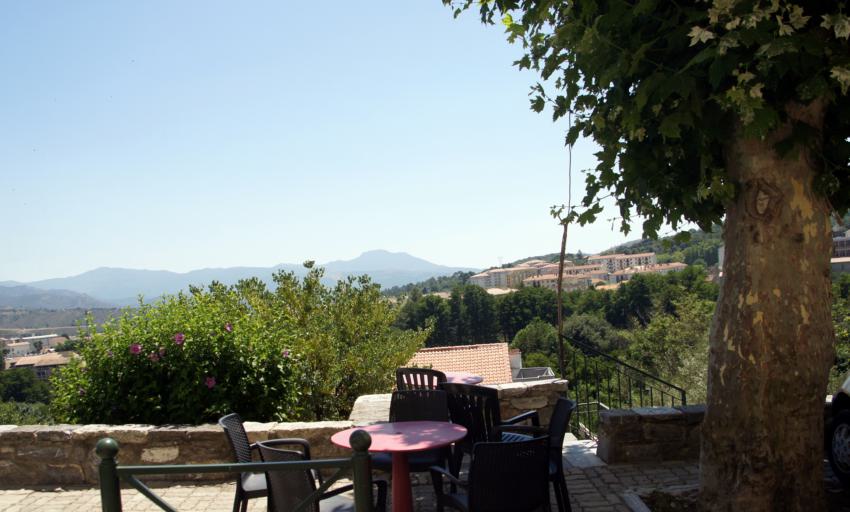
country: FR
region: Corsica
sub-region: Departement de la Haute-Corse
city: Corte
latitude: 42.3069
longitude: 9.1507
